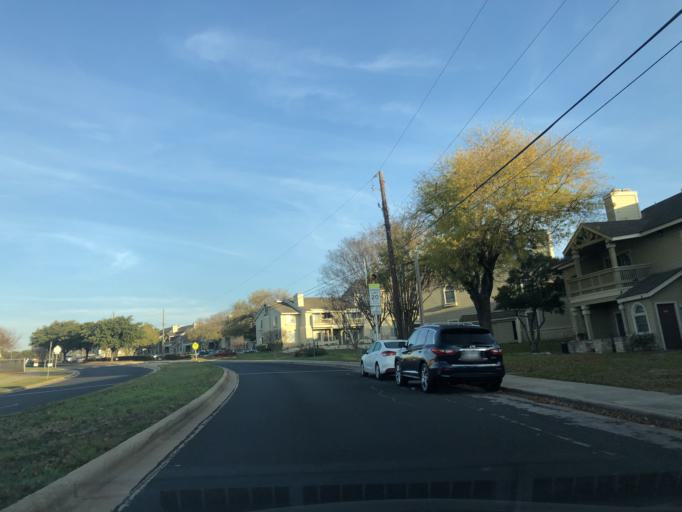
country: US
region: Texas
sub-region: Travis County
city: Wells Branch
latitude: 30.4315
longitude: -97.6748
